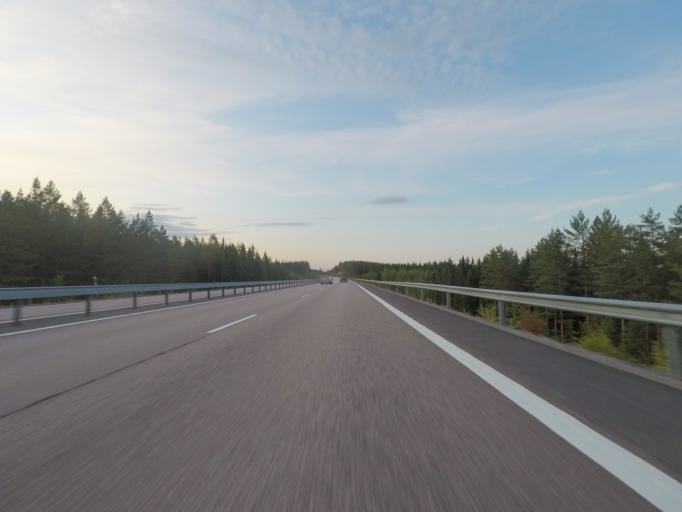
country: FI
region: Central Finland
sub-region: Jyvaeskylae
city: Saeynaetsalo
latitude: 62.1642
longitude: 25.9012
